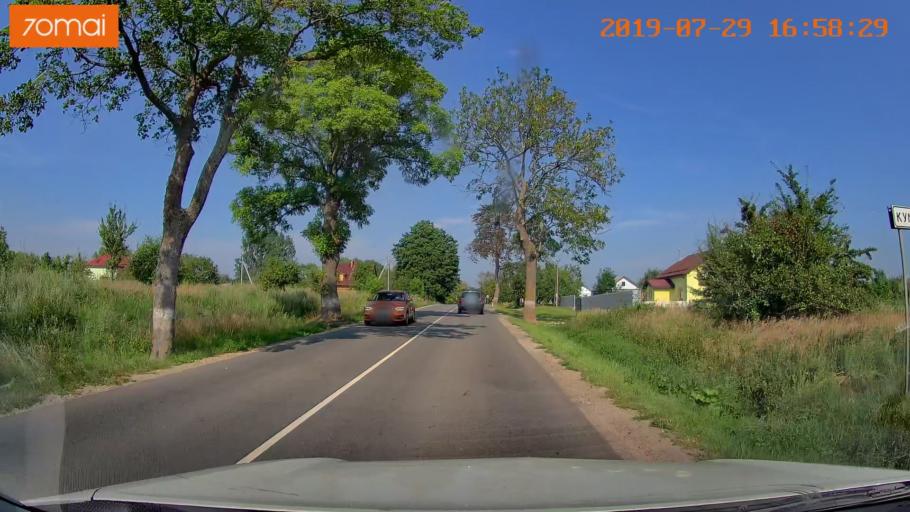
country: RU
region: Kaliningrad
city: Volochayevskoye
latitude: 54.8172
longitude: 20.2037
